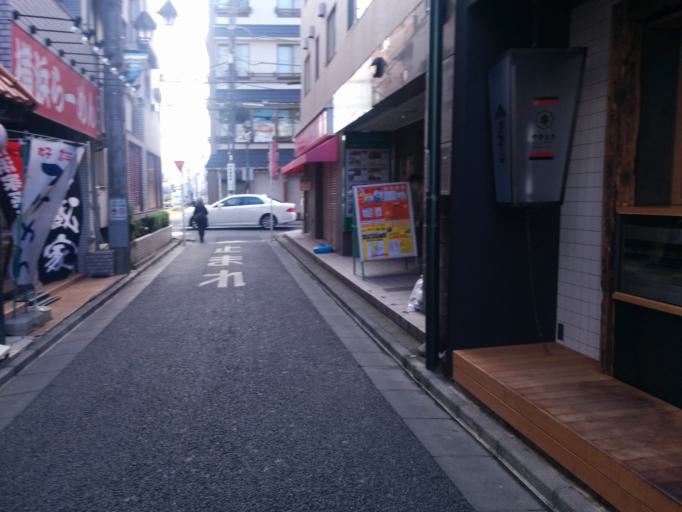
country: JP
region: Tokyo
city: Chofugaoka
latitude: 35.6335
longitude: 139.5345
